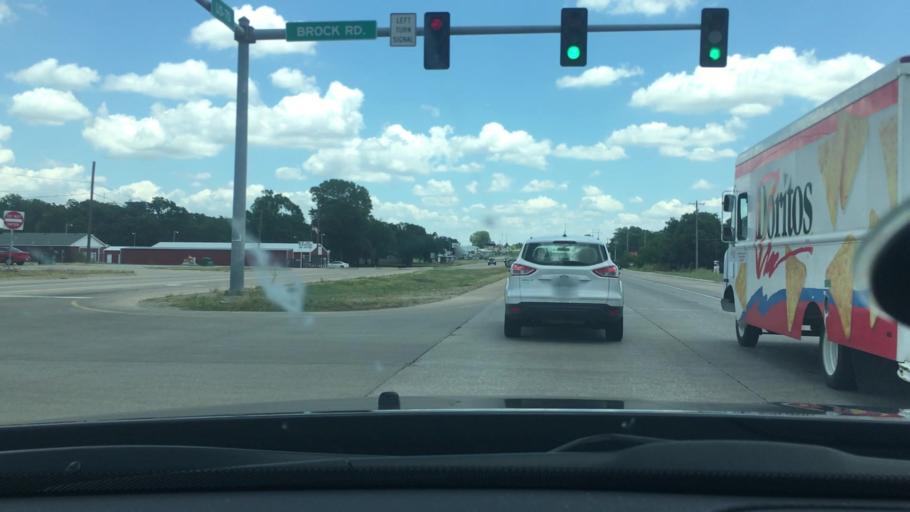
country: US
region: Oklahoma
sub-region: Carter County
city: Lone Grove
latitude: 34.1728
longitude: -97.2305
